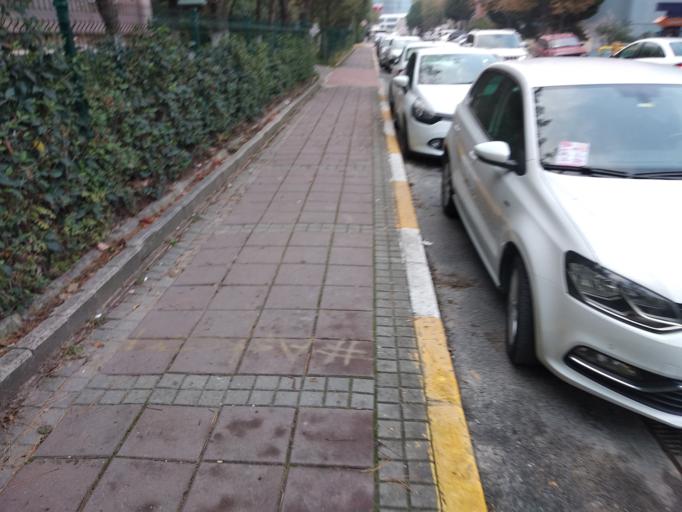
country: TR
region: Istanbul
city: Beylikduezue
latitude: 41.0108
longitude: 28.6498
